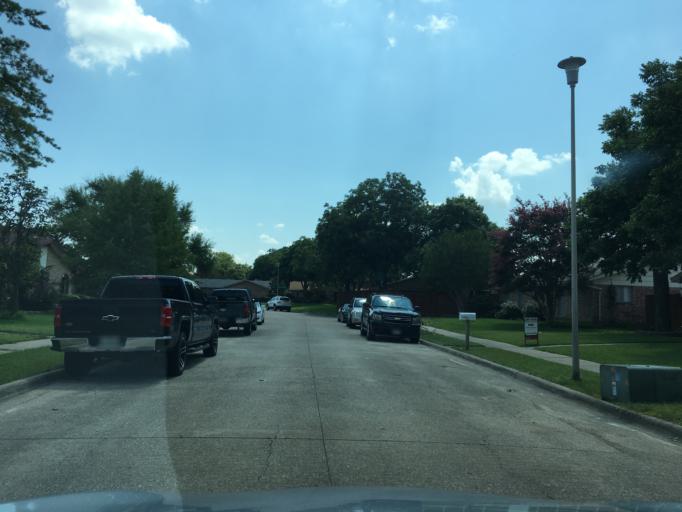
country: US
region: Texas
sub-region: Dallas County
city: Garland
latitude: 32.9443
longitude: -96.6614
